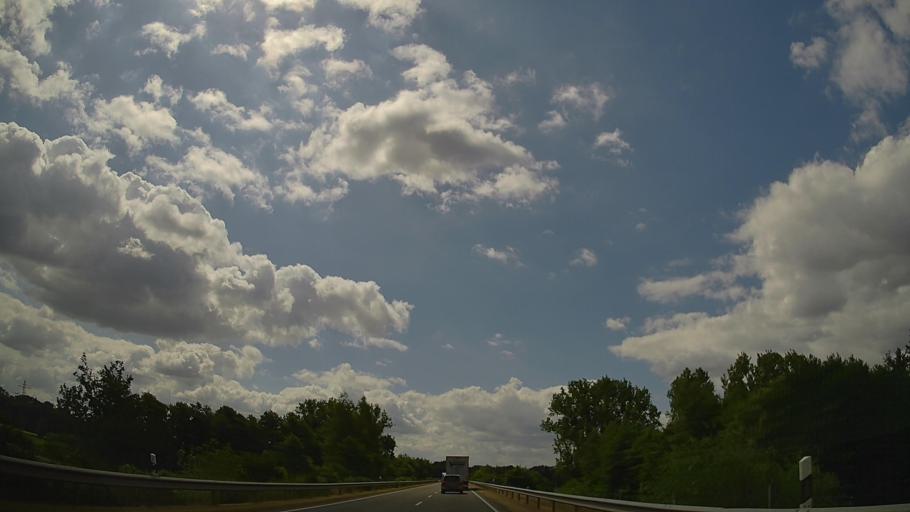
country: DE
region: Lower Saxony
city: Vechta
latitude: 52.7108
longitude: 8.2622
